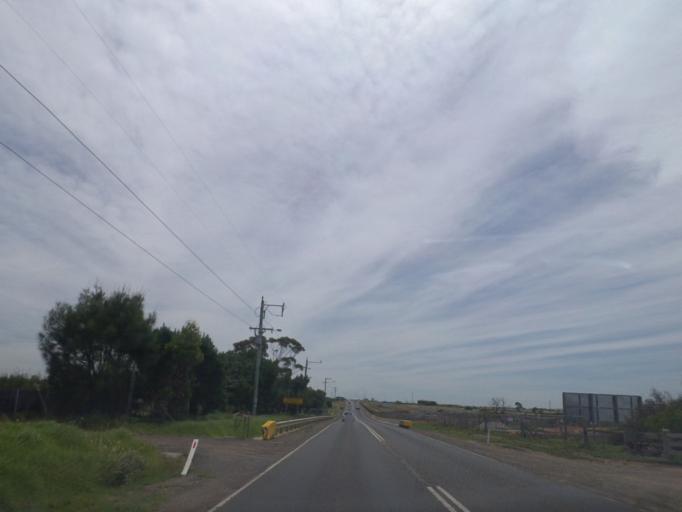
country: AU
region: Victoria
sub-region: Wyndham
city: Tarneit
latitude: -37.8239
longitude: 144.6929
